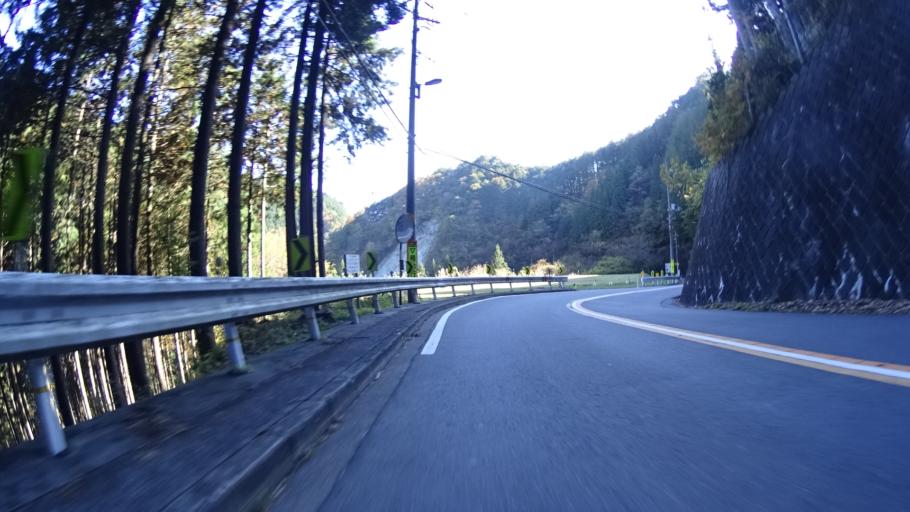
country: JP
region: Yamanashi
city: Uenohara
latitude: 35.7183
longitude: 139.0706
